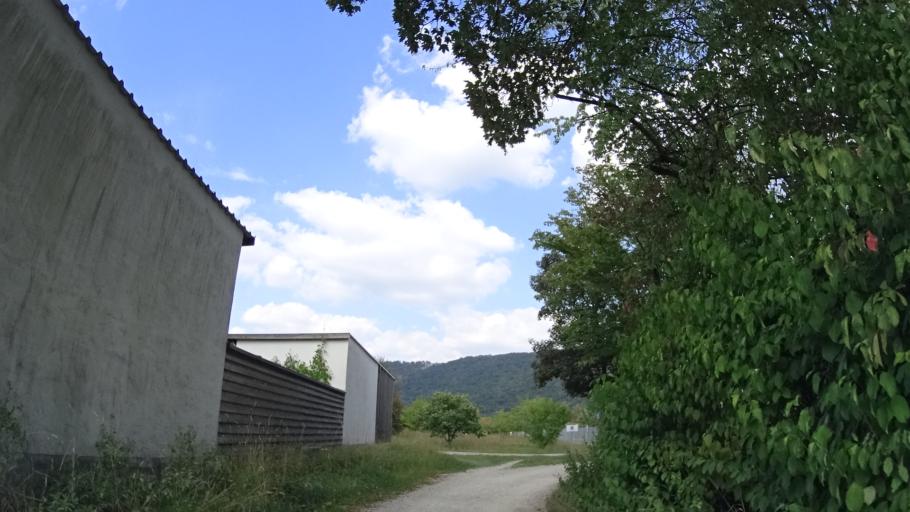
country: DE
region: Bavaria
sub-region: Lower Bavaria
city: Riedenburg
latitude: 48.9765
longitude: 11.6893
